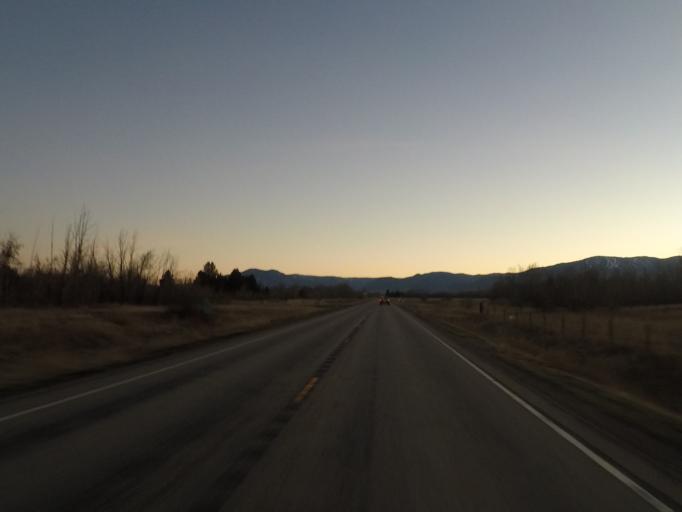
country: US
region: Montana
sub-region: Carbon County
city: Red Lodge
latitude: 45.2898
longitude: -109.2099
